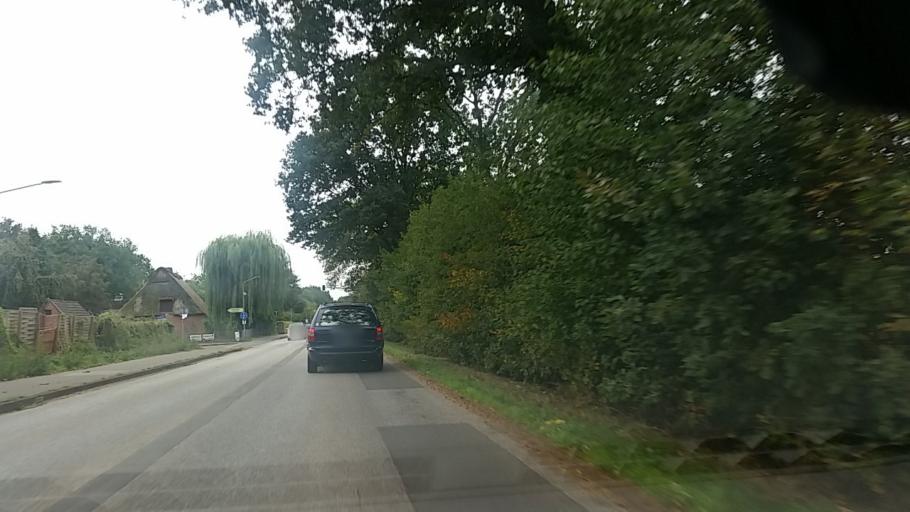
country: DE
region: Schleswig-Holstein
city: Kayhude
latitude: 53.7579
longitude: 10.1297
